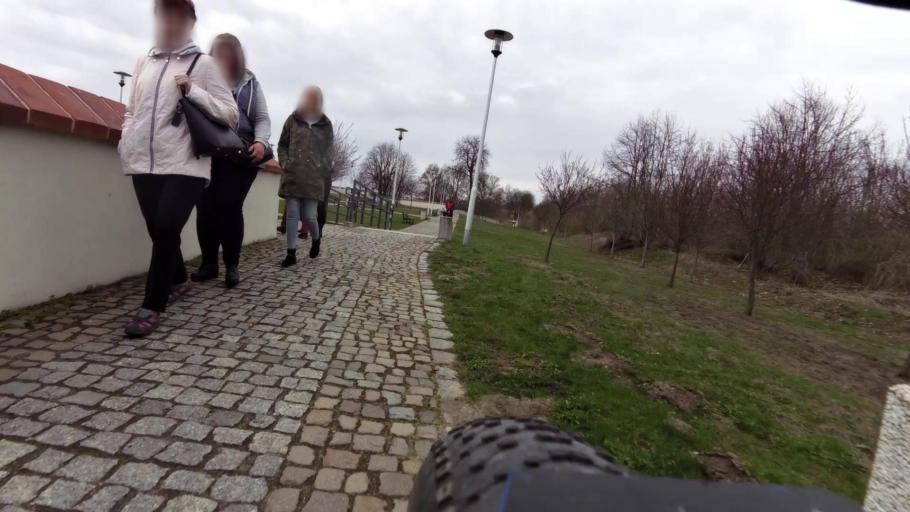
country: PL
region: Lubusz
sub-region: Powiat gorzowski
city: Kostrzyn nad Odra
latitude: 52.5778
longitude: 14.6352
